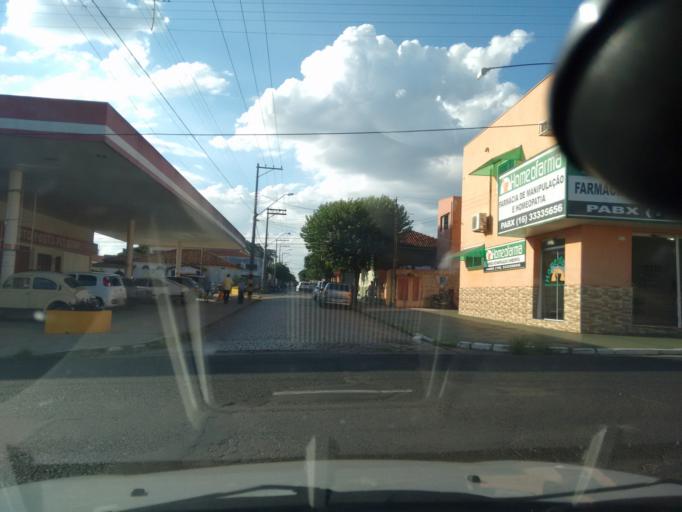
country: BR
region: Sao Paulo
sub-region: Araraquara
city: Araraquara
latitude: -21.7920
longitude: -48.1656
